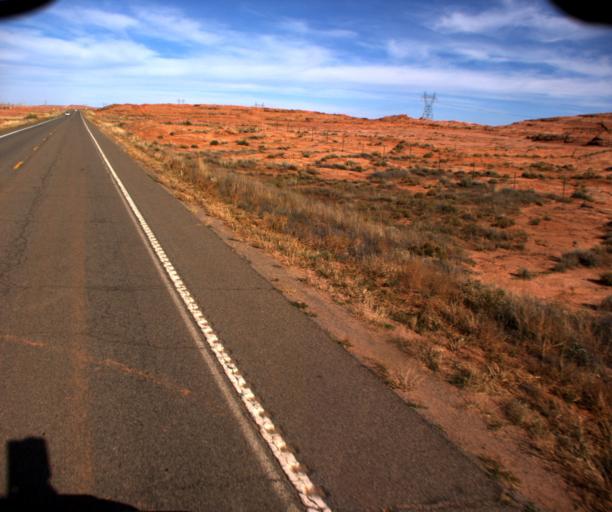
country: US
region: Arizona
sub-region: Navajo County
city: Kayenta
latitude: 36.8306
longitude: -109.8585
